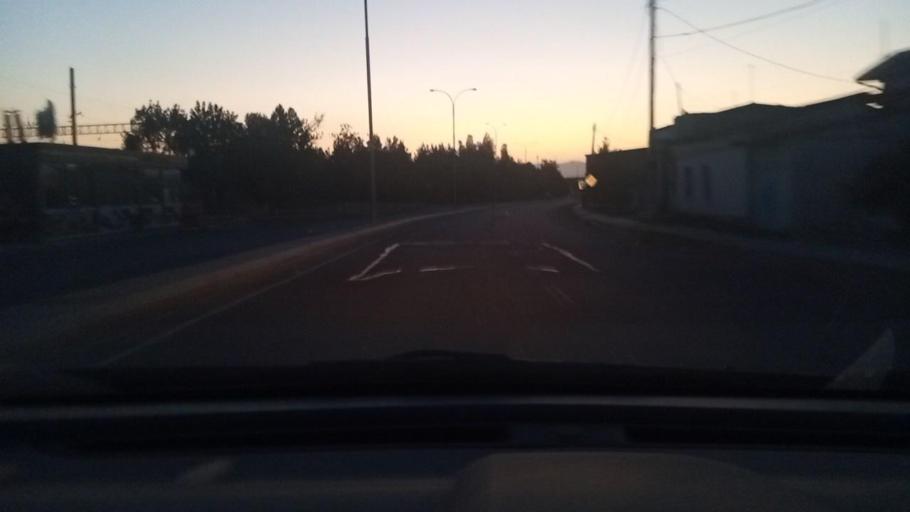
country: UZ
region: Toshkent Shahri
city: Tashkent
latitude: 41.2462
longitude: 69.2044
